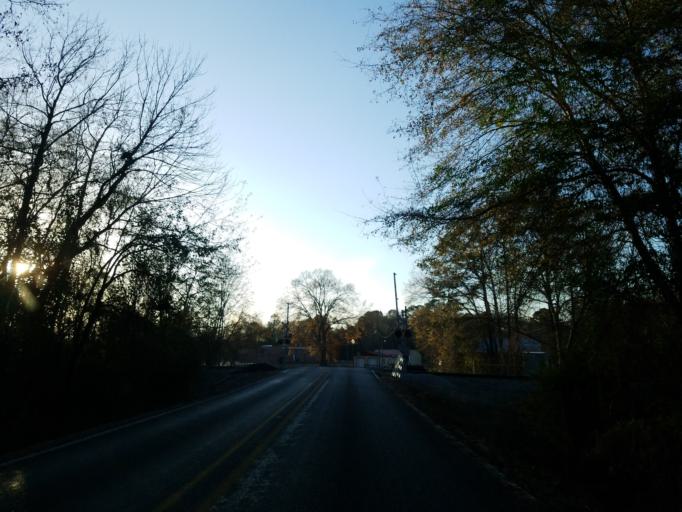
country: US
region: Mississippi
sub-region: Clarke County
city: Stonewall
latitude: 32.1758
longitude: -88.8278
